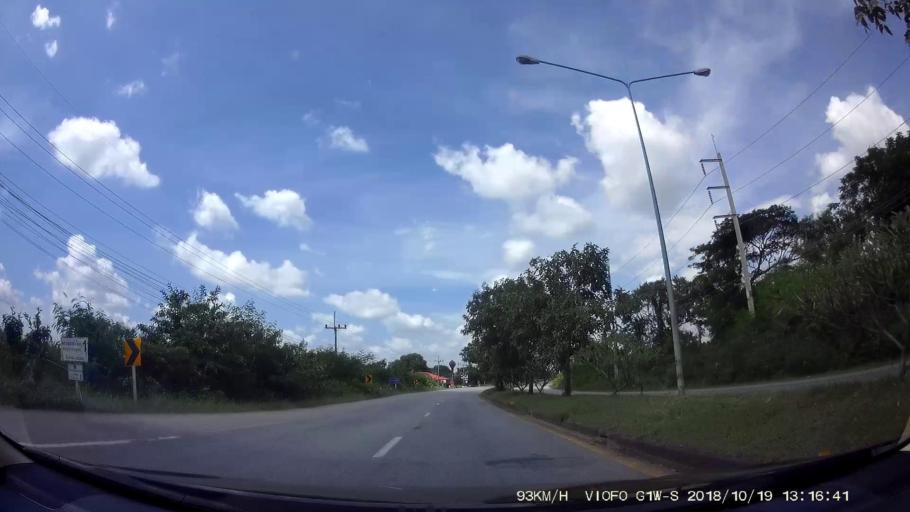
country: TH
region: Chaiyaphum
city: Chatturat
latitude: 15.4071
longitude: 101.8347
